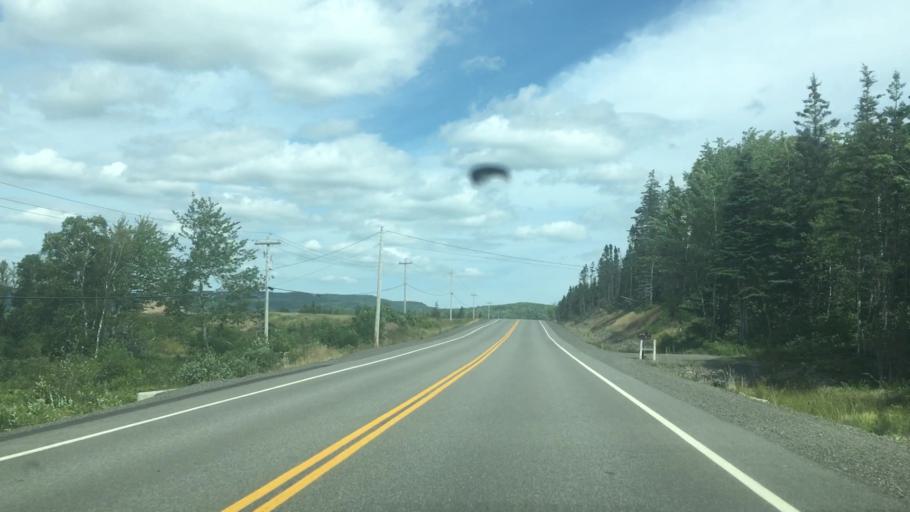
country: CA
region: Nova Scotia
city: Sydney Mines
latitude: 46.3291
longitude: -60.6028
